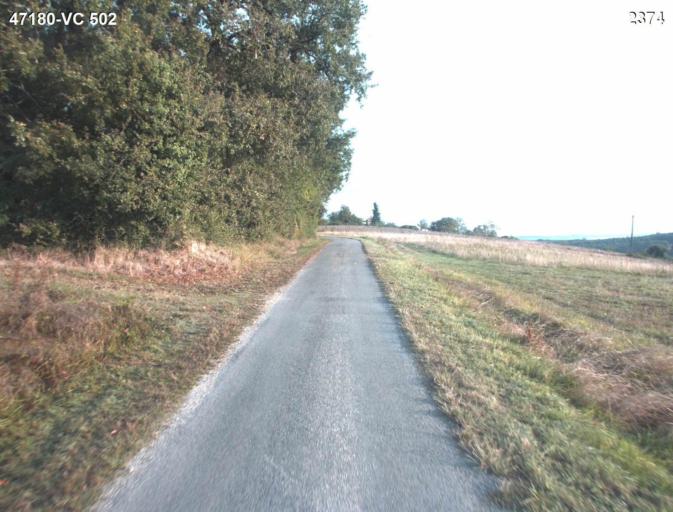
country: FR
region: Aquitaine
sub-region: Departement du Lot-et-Garonne
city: Sainte-Colombe-en-Bruilhois
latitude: 44.1781
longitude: 0.4831
